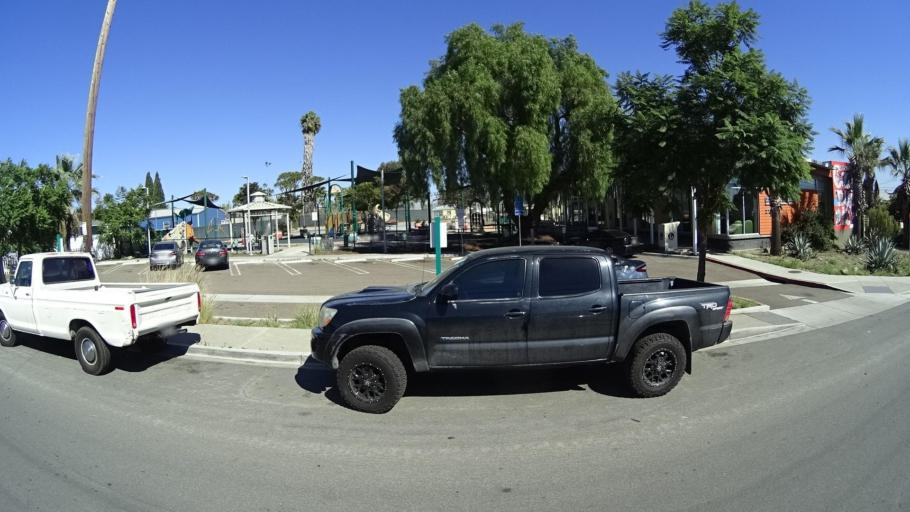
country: US
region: California
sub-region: San Diego County
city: Chula Vista
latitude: 32.6667
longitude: -117.0715
